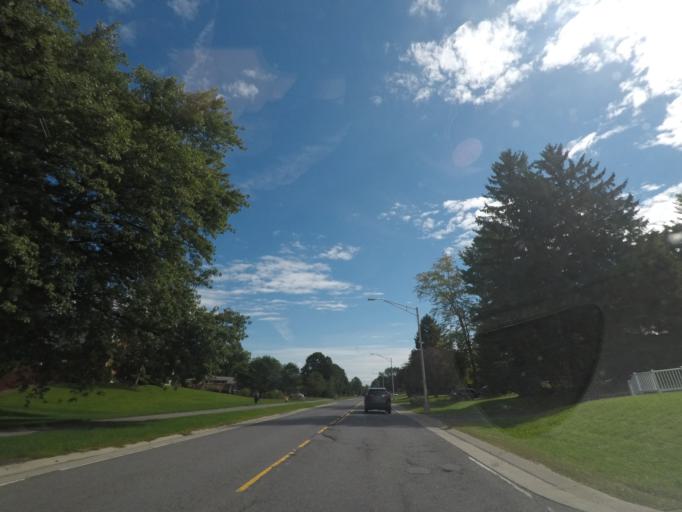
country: US
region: New York
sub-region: Albany County
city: West Albany
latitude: 42.6494
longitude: -73.7967
